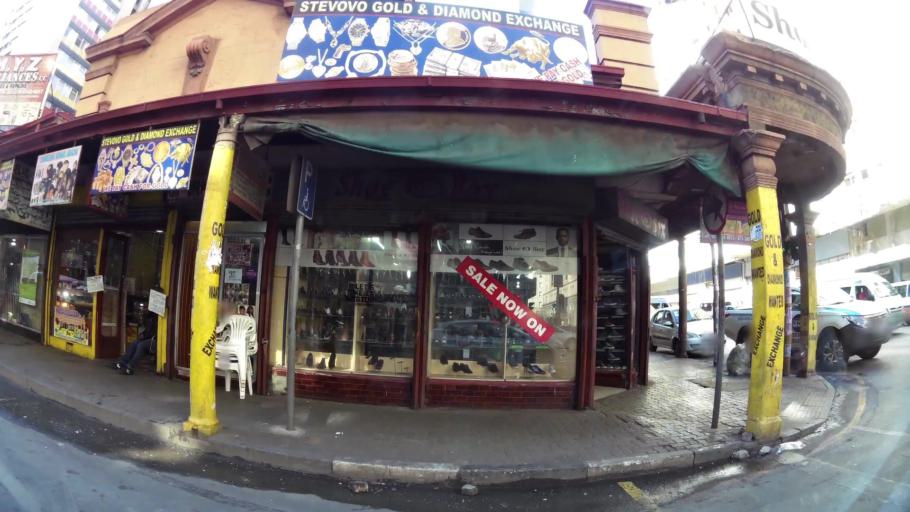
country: ZA
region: Gauteng
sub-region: City of Johannesburg Metropolitan Municipality
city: Johannesburg
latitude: -26.2018
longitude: 28.0403
